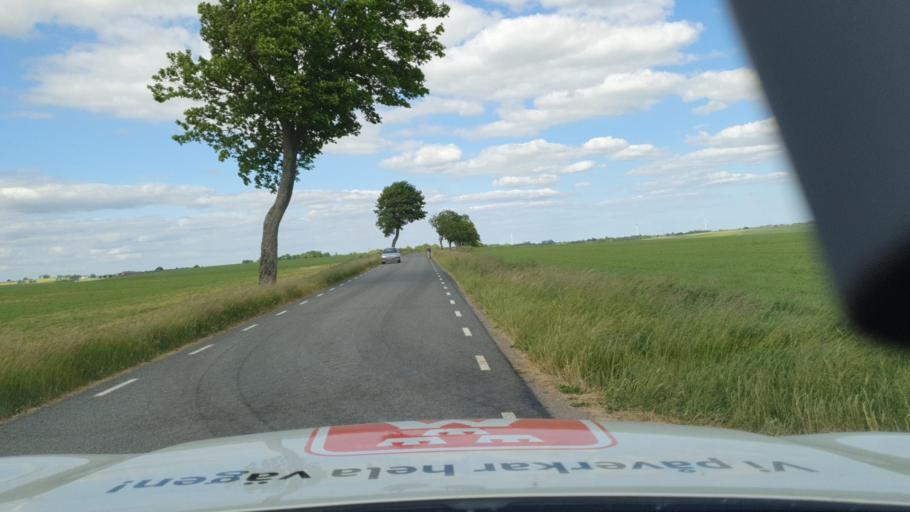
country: SE
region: Skane
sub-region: Tomelilla Kommun
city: Tomelilla
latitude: 55.4829
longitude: 14.0305
